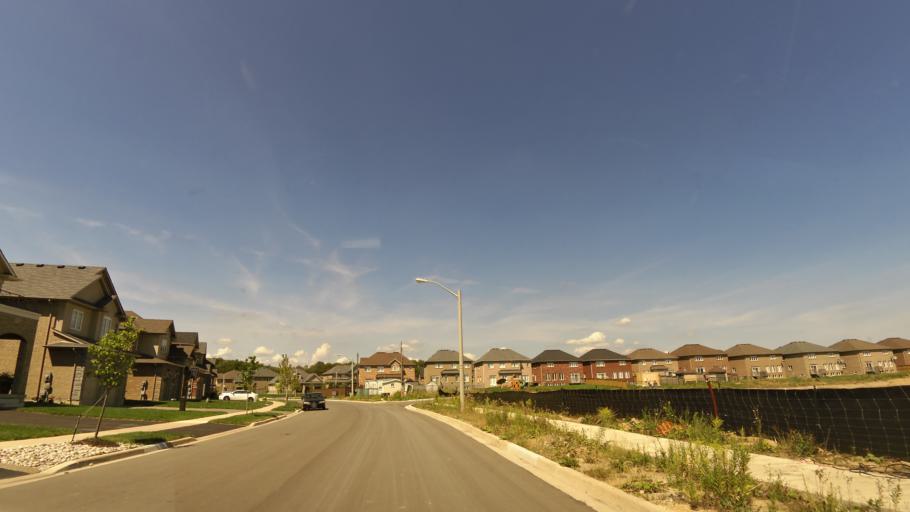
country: CA
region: Ontario
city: Ancaster
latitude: 43.2146
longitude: -79.9349
